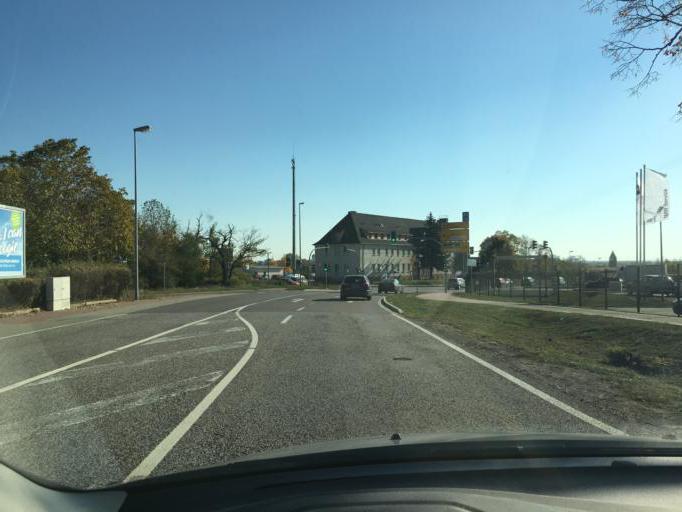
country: DE
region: Saxony-Anhalt
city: Bernburg
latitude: 51.8093
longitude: 11.7250
